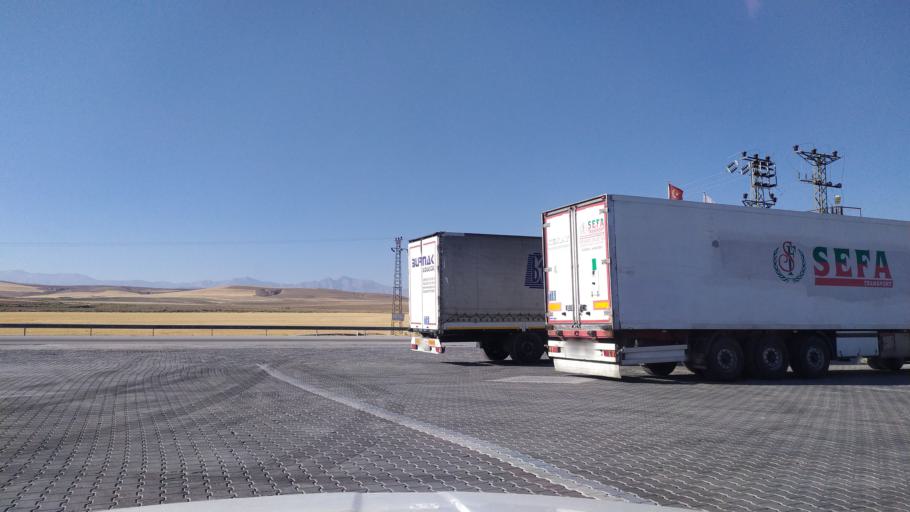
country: TR
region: Nigde
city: Ulukisla
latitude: 37.6356
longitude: 34.3139
